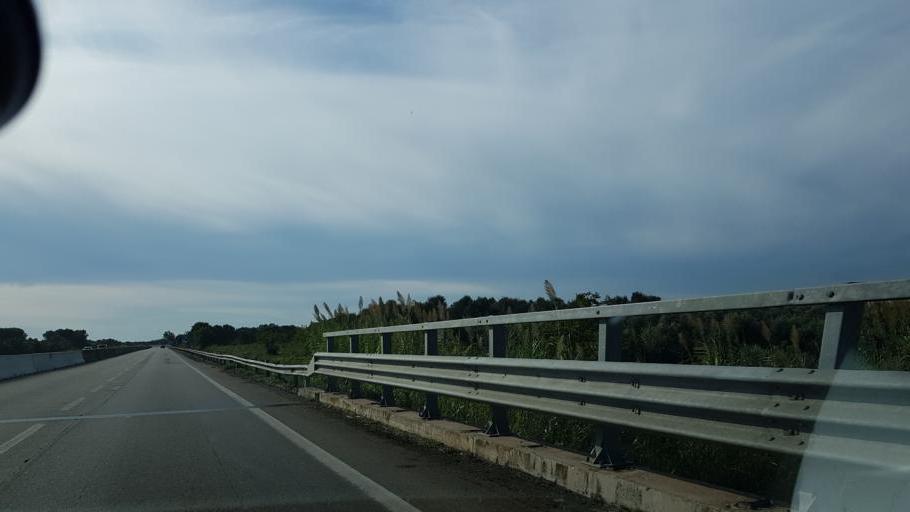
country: IT
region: Apulia
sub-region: Provincia di Brindisi
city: Tuturano
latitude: 40.5469
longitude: 17.9991
